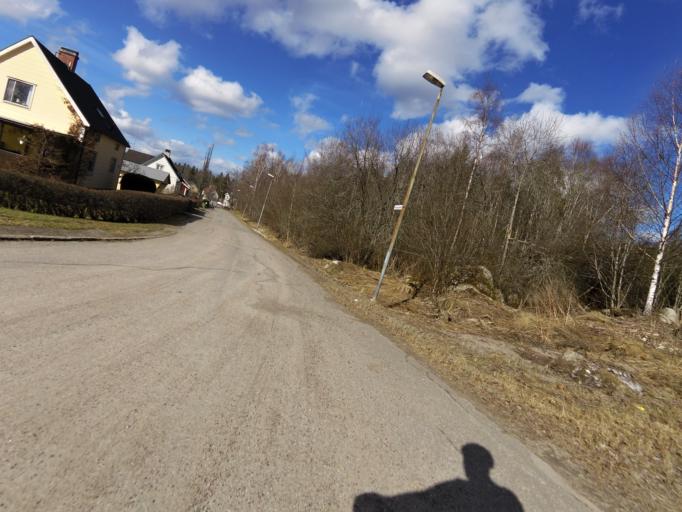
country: SE
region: Gaevleborg
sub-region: Hofors Kommun
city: Hofors
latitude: 60.5413
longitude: 16.3143
